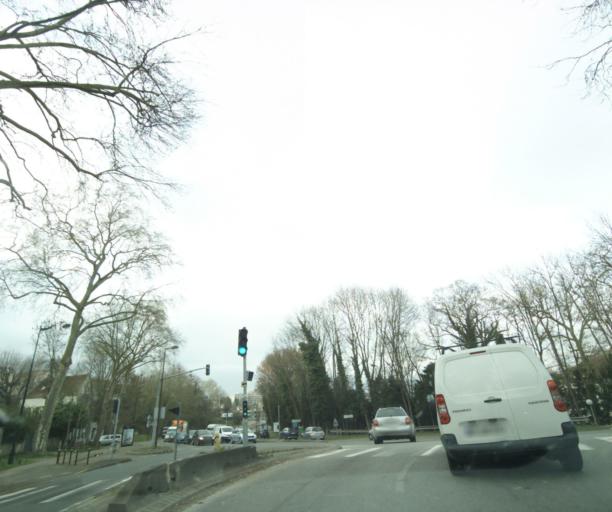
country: FR
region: Ile-de-France
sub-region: Departement des Yvelines
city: Louveciennes
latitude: 48.8725
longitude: 2.1020
